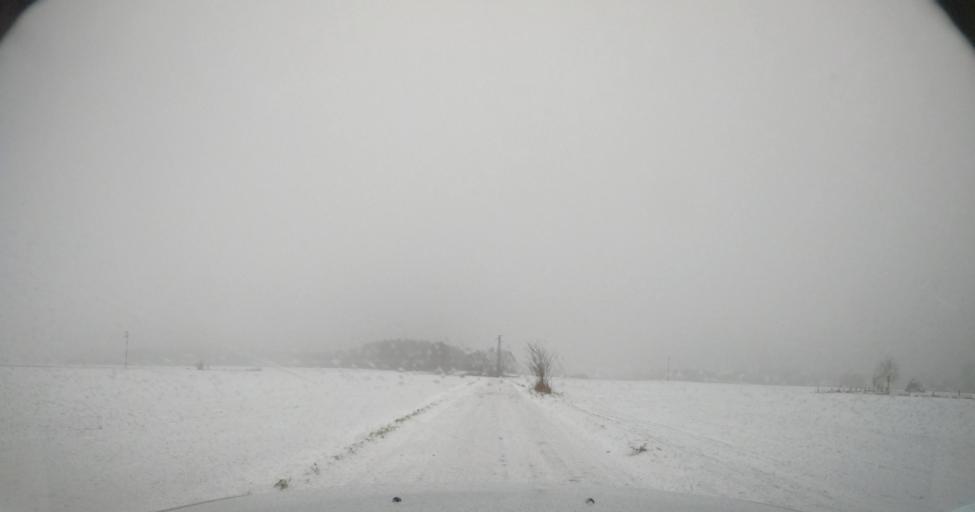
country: PL
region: West Pomeranian Voivodeship
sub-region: Powiat kamienski
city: Golczewo
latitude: 53.7688
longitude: 14.9137
